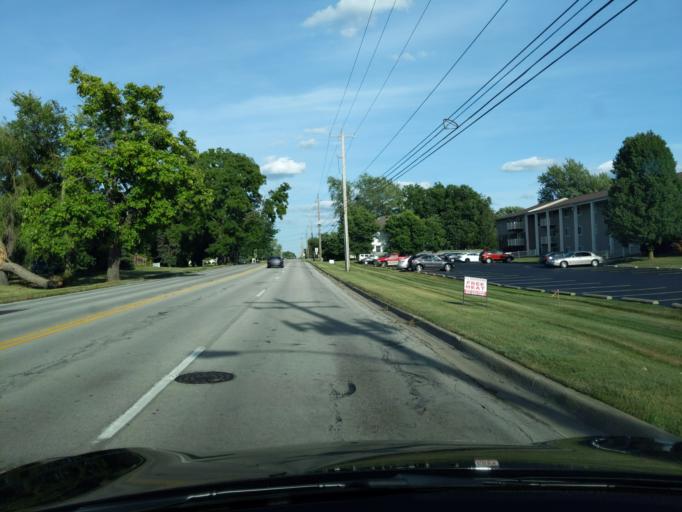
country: US
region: Michigan
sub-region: Eaton County
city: Waverly
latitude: 42.7265
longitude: -84.6318
